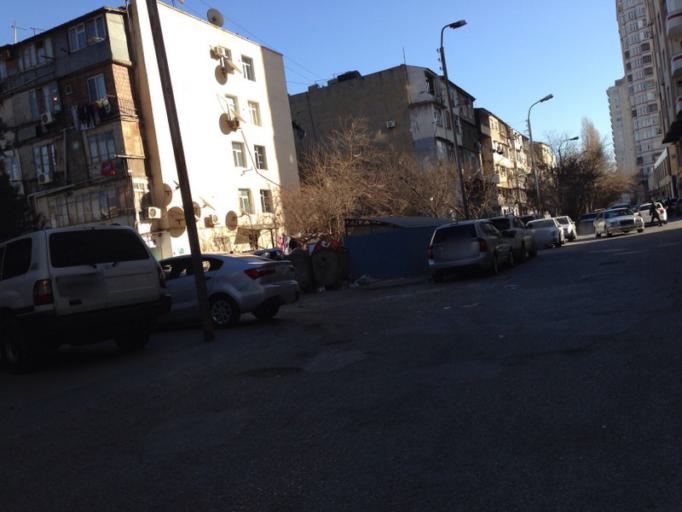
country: AZ
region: Baki
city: Baku
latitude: 40.4029
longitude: 49.8650
